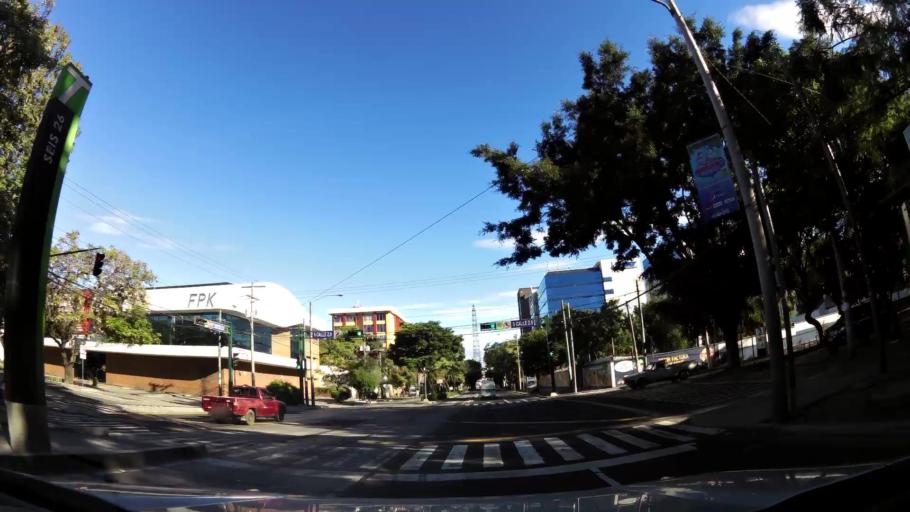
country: GT
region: Guatemala
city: Guatemala City
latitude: 14.6095
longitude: -90.5173
